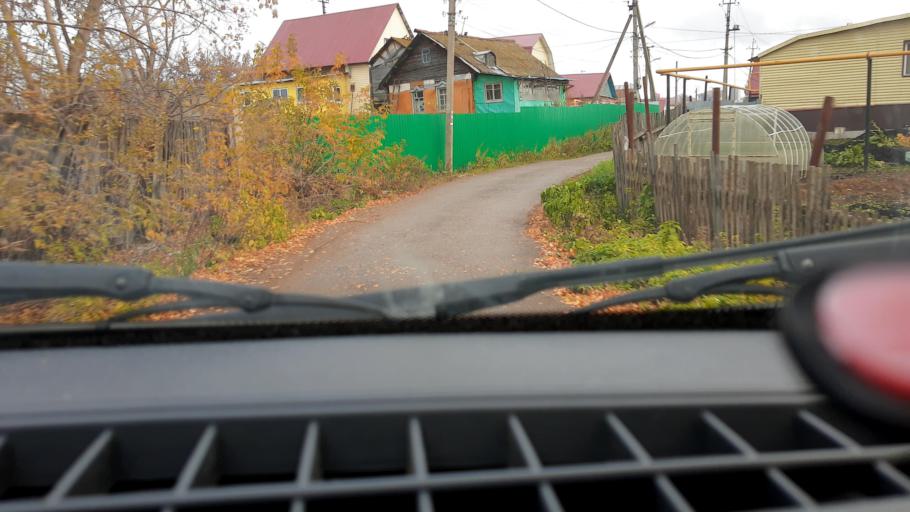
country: RU
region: Bashkortostan
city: Mikhaylovka
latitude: 54.7497
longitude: 55.9063
